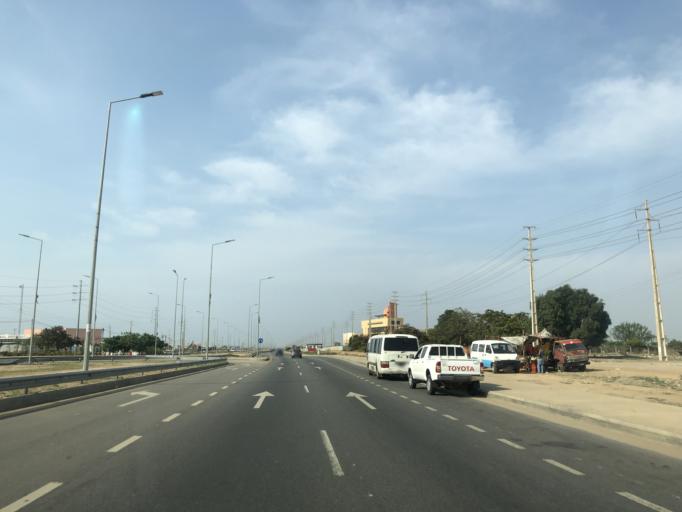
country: AO
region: Luanda
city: Luanda
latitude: -8.9665
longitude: 13.2557
